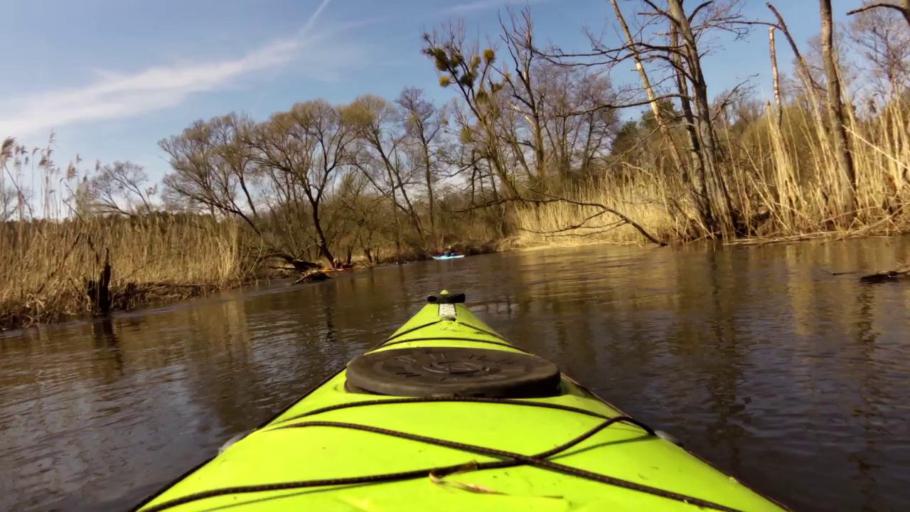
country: PL
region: West Pomeranian Voivodeship
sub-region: Powiat lobeski
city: Lobez
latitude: 53.6531
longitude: 15.5624
